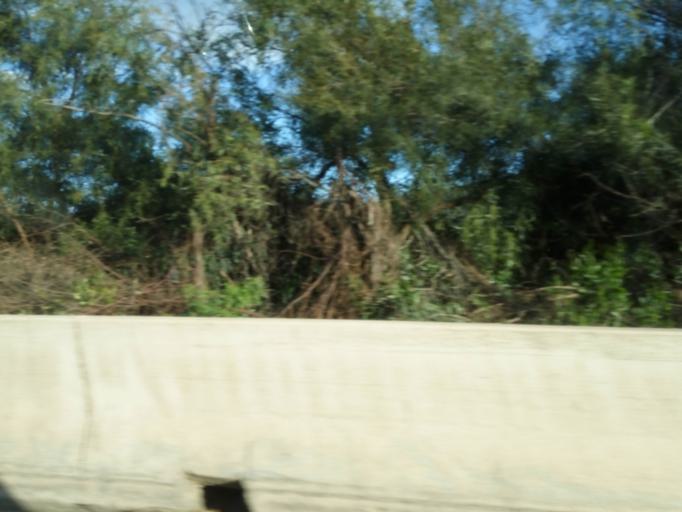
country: DZ
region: Tipaza
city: El Affroun
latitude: 36.4452
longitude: 2.5870
